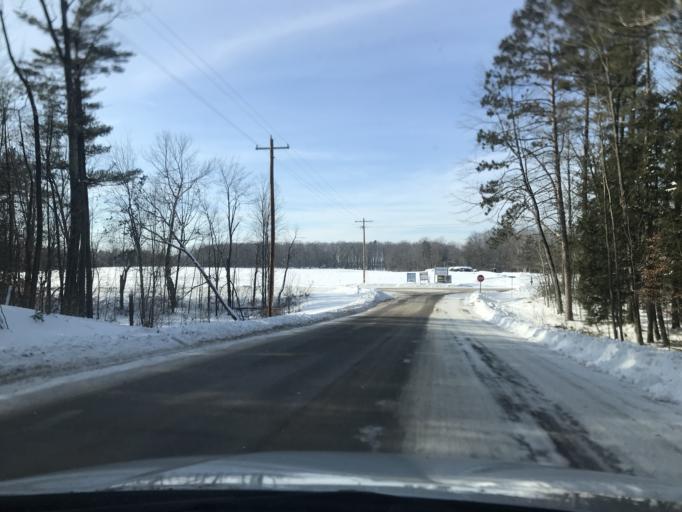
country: US
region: Wisconsin
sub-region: Oconto County
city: Oconto Falls
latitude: 45.1477
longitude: -88.1868
